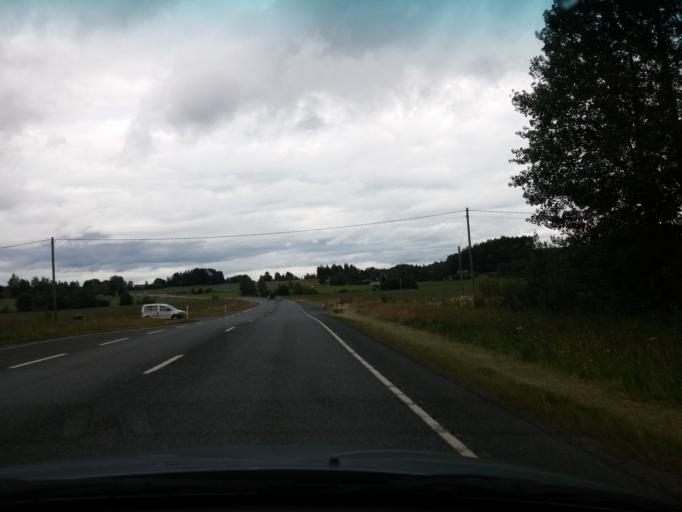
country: FI
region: Uusimaa
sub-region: Porvoo
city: Askola
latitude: 60.4407
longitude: 25.5809
